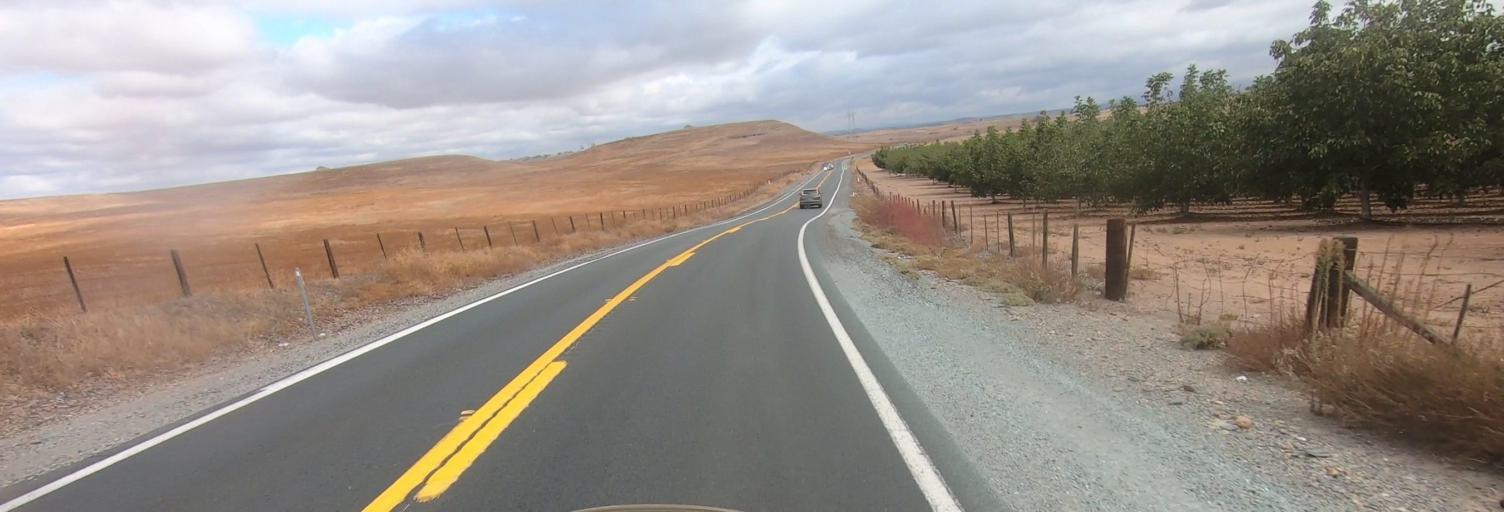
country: US
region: California
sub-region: San Joaquin County
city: Linden
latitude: 38.0755
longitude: -120.9801
